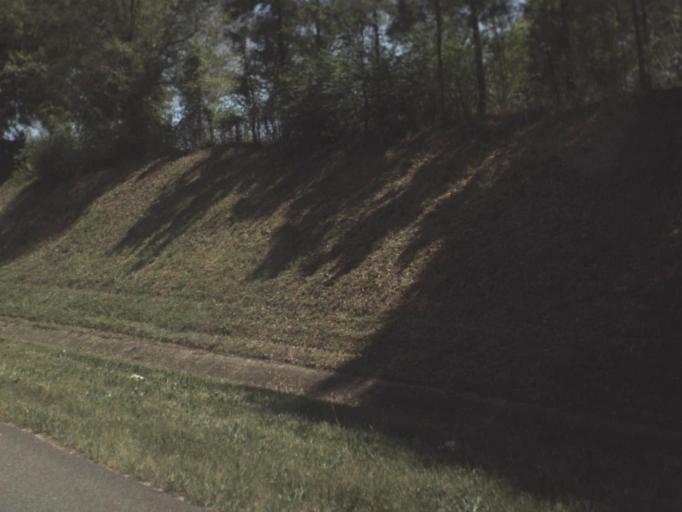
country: US
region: Florida
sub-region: Escambia County
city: Century
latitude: 30.9487
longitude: -87.1848
